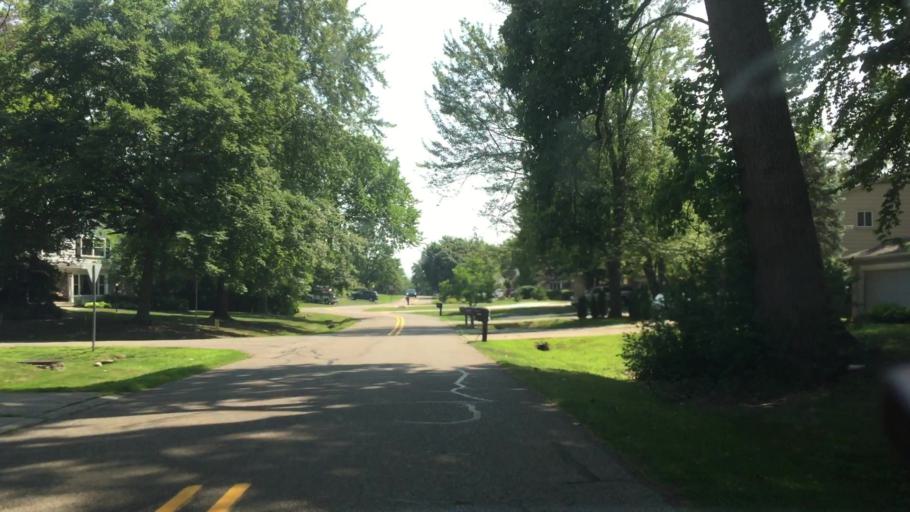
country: US
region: Michigan
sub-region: Oakland County
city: West Bloomfield Township
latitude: 42.5348
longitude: -83.3550
